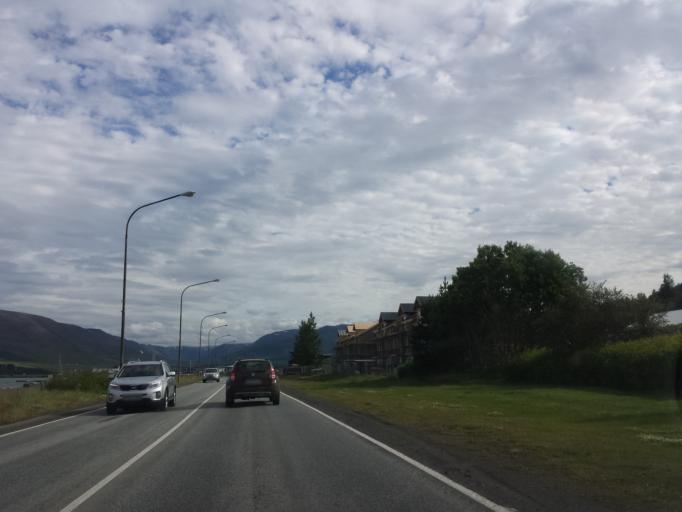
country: IS
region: Northeast
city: Akureyri
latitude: 65.6748
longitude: -18.0871
